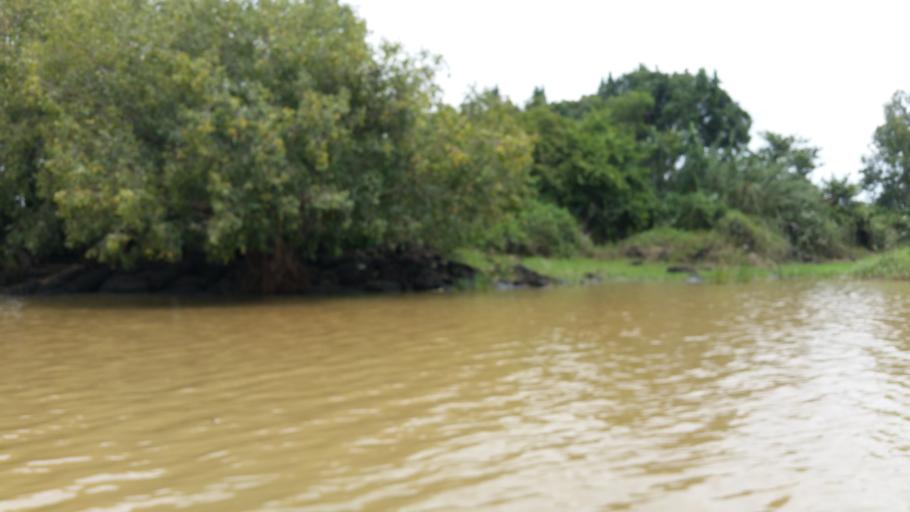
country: ET
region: Amhara
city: Bahir Dar
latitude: 11.6207
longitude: 37.4046
